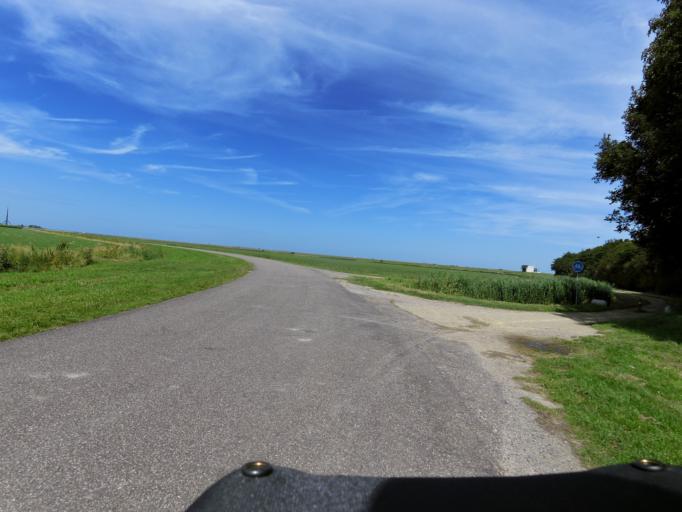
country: NL
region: South Holland
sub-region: Gemeente Goeree-Overflakkee
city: Dirksland
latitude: 51.7902
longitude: 4.1166
